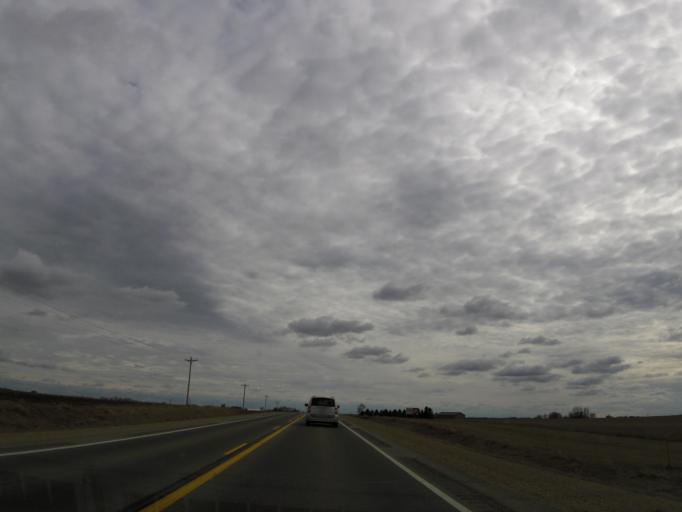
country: US
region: Iowa
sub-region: Chickasaw County
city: New Hampton
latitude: 43.1490
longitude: -92.2989
